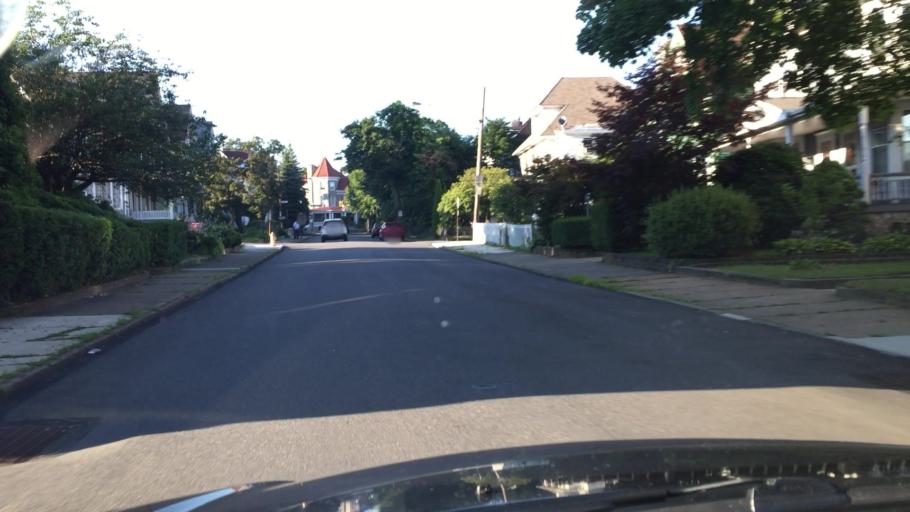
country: US
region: Pennsylvania
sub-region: Luzerne County
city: Hazleton
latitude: 40.9589
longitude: -75.9734
